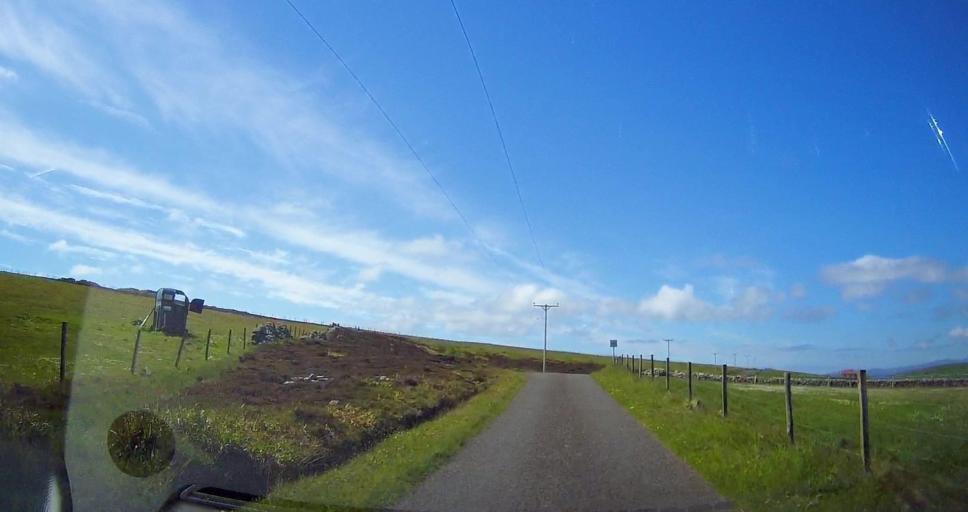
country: GB
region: Scotland
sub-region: Orkney Islands
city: Orkney
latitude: 58.8569
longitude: -2.9428
